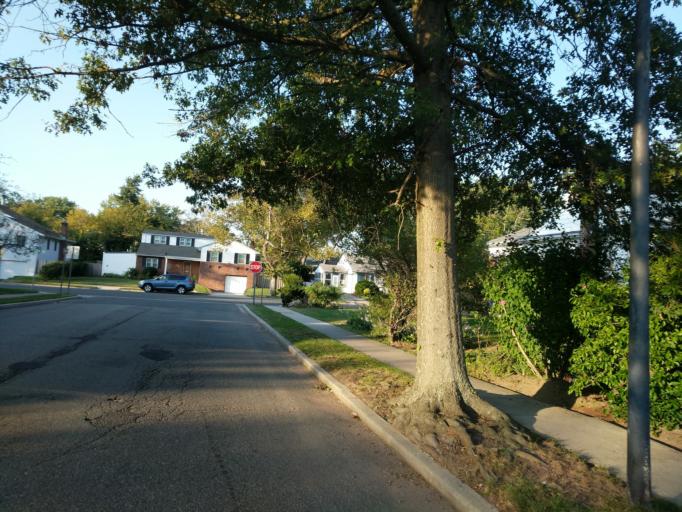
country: US
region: New York
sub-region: Nassau County
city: South Valley Stream
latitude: 40.6564
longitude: -73.7211
